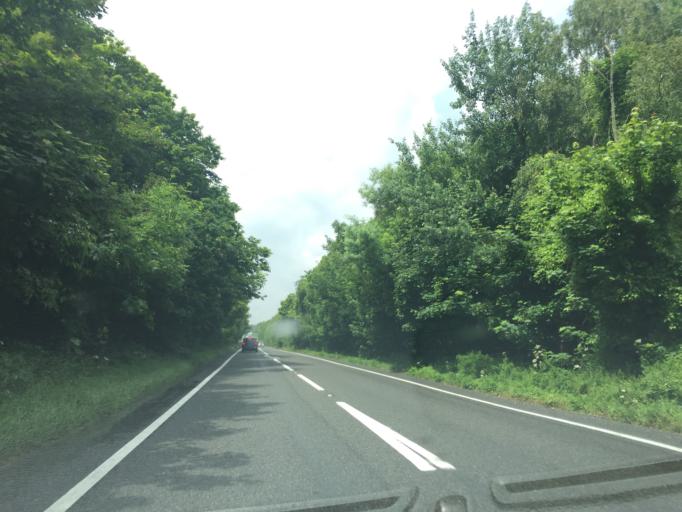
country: GB
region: England
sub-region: Dorset
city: Wareham
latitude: 50.6464
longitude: -2.0699
